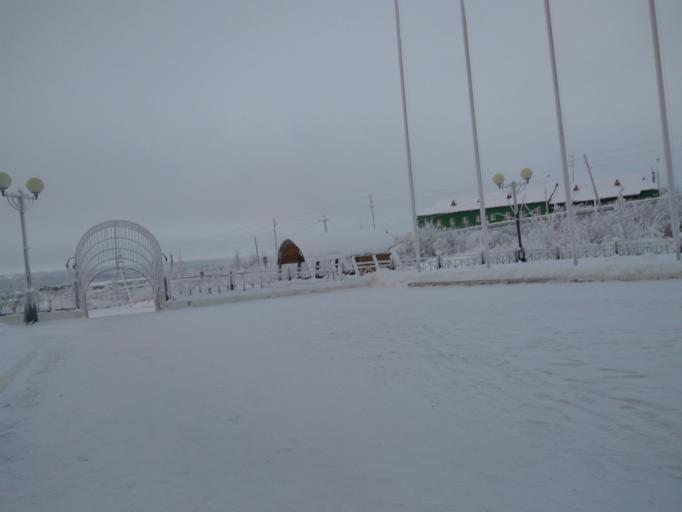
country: RU
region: Sakha
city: Aykhal
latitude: 65.9341
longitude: 111.5151
